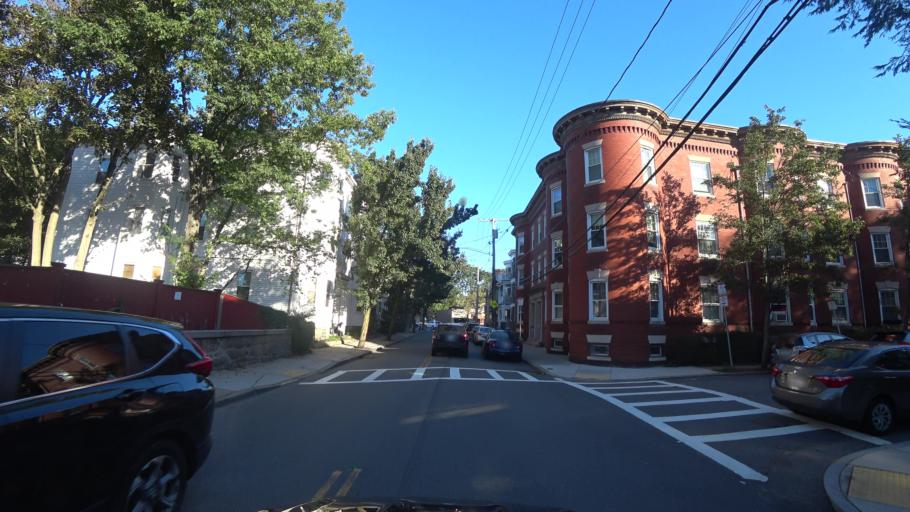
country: US
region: Massachusetts
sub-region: Suffolk County
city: Jamaica Plain
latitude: 42.3150
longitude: -71.1153
